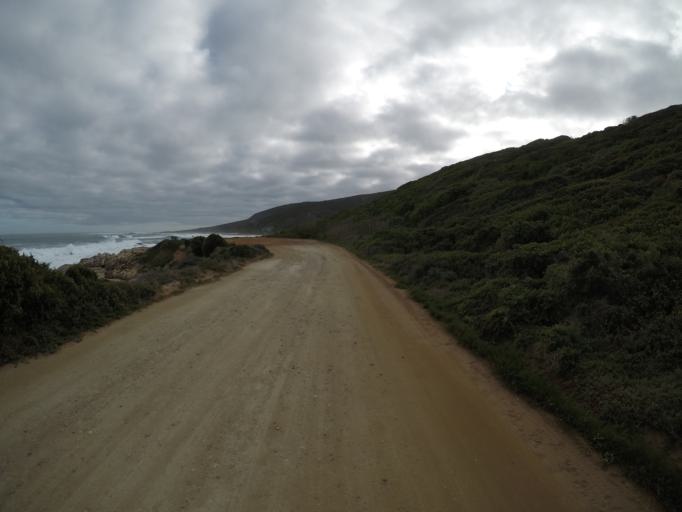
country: ZA
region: Western Cape
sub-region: Eden District Municipality
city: Riversdale
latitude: -34.4320
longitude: 21.3248
